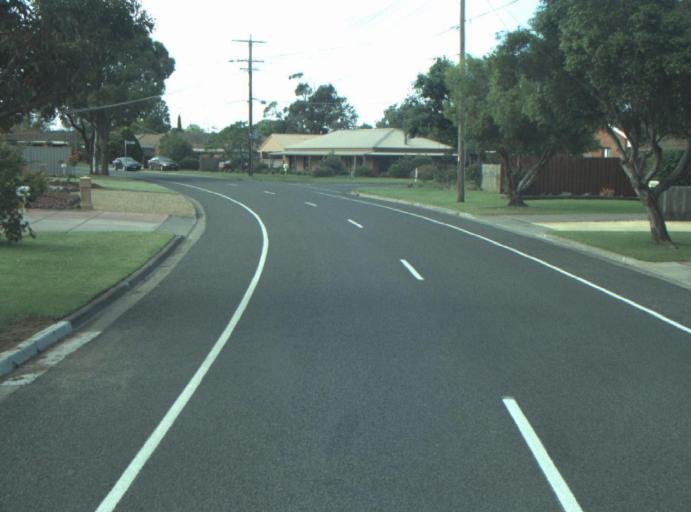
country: AU
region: Victoria
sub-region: Greater Geelong
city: Lara
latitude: -38.0175
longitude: 144.3860
